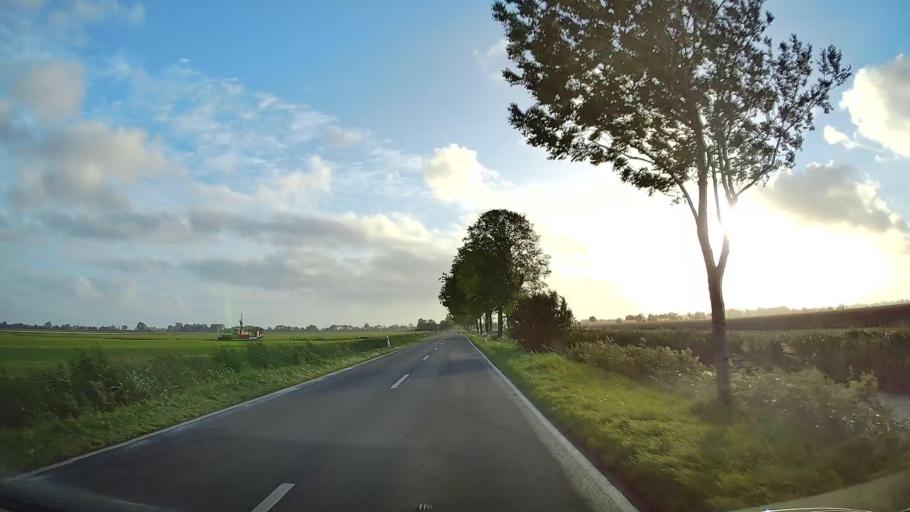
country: DE
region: Schleswig-Holstein
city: Suderau
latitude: 53.7967
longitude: 9.5171
